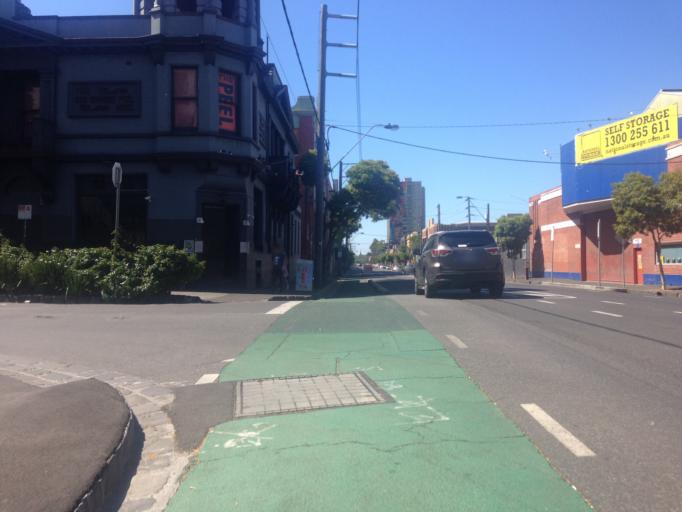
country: AU
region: Victoria
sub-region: Yarra
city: Collingwood
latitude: -37.8055
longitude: 144.9862
